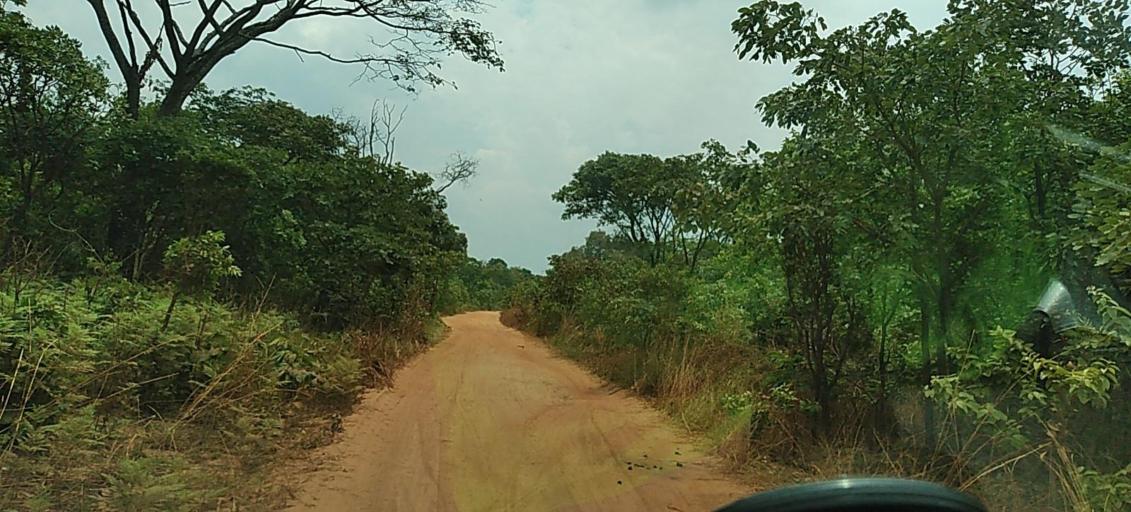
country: ZM
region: North-Western
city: Kansanshi
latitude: -12.0498
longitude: 26.3393
